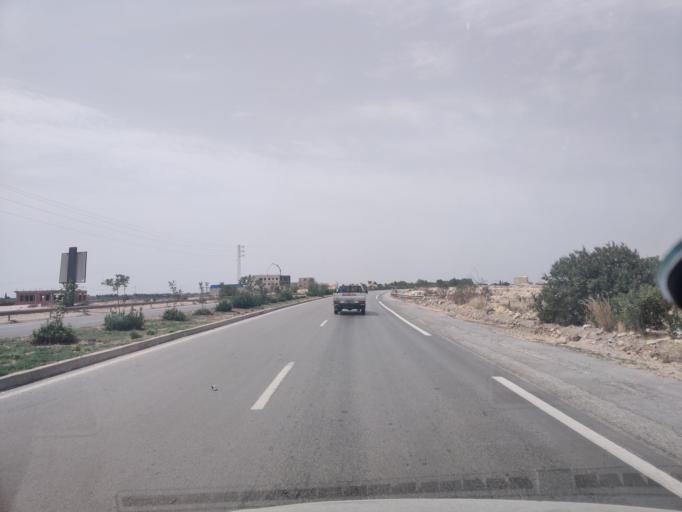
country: TN
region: Susah
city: Akouda
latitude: 35.8358
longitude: 10.5465
